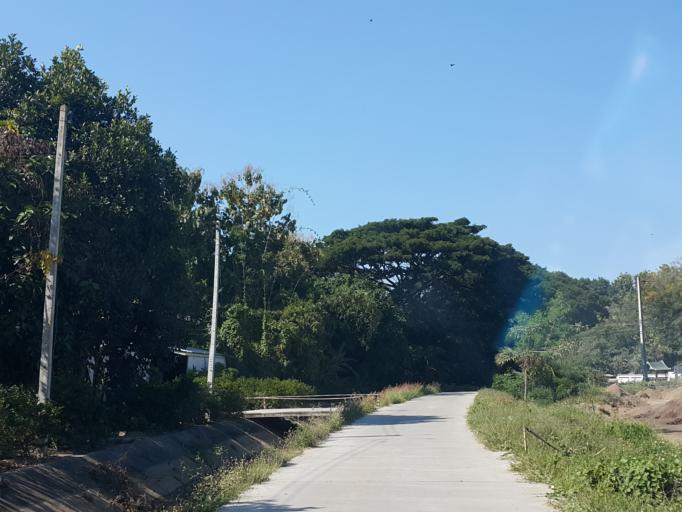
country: TH
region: Chiang Mai
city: San Sai
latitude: 18.8650
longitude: 98.9843
